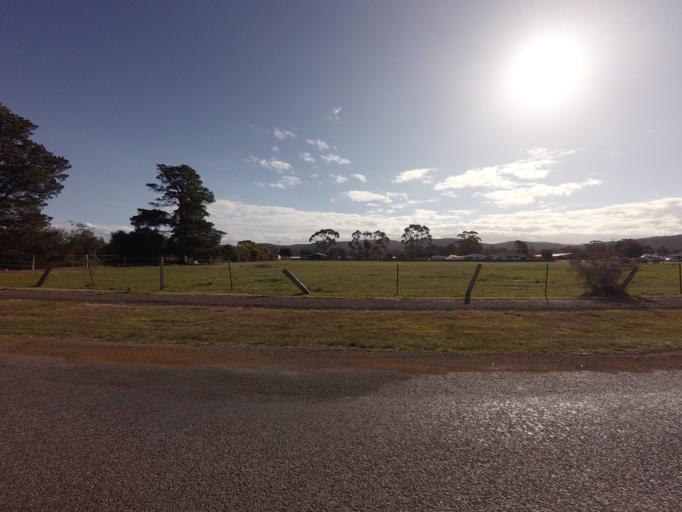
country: AU
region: Tasmania
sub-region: Sorell
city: Sorell
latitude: -42.5026
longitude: 147.9153
